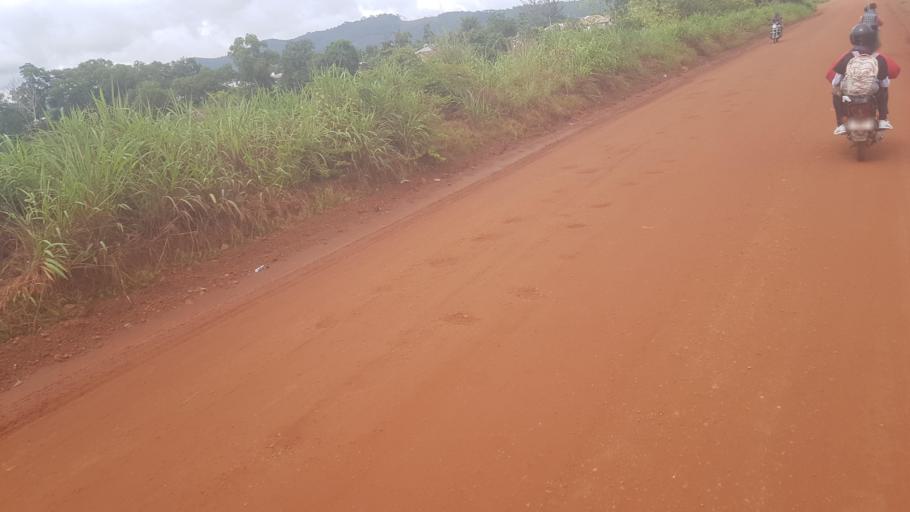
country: SL
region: Southern Province
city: Mogbwemo
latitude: 7.7641
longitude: -12.3033
